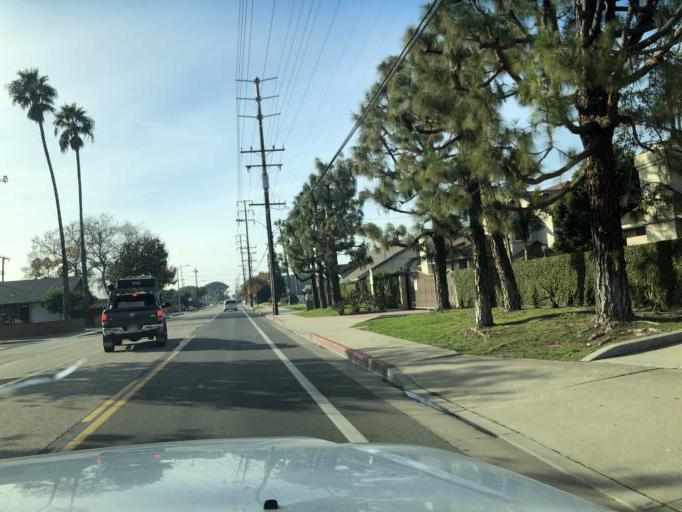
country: US
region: California
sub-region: Orange County
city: Costa Mesa
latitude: 33.6561
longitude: -117.9290
